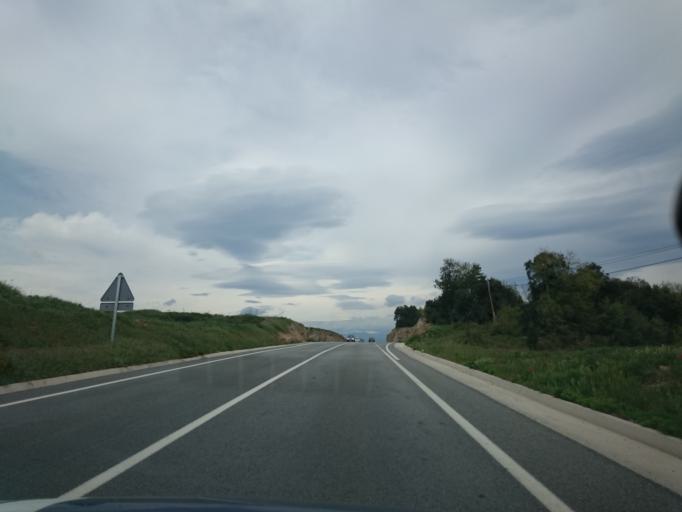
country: ES
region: Catalonia
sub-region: Provincia de Barcelona
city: Olost
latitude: 41.9963
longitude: 2.0945
